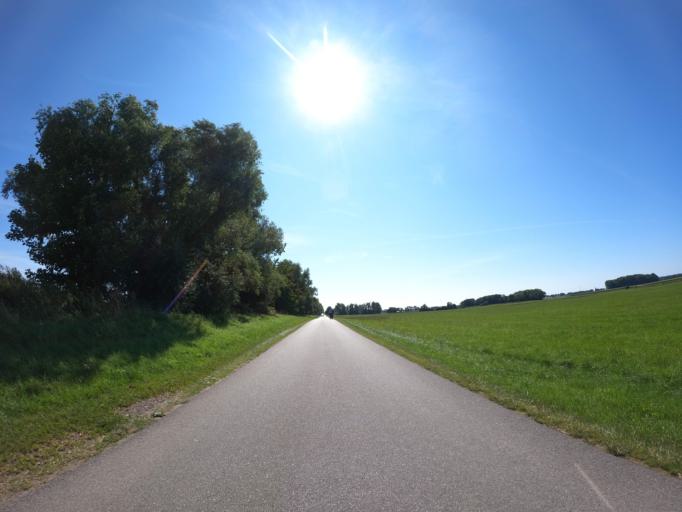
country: DE
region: Mecklenburg-Vorpommern
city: Prohn
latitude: 54.3908
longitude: 13.0298
